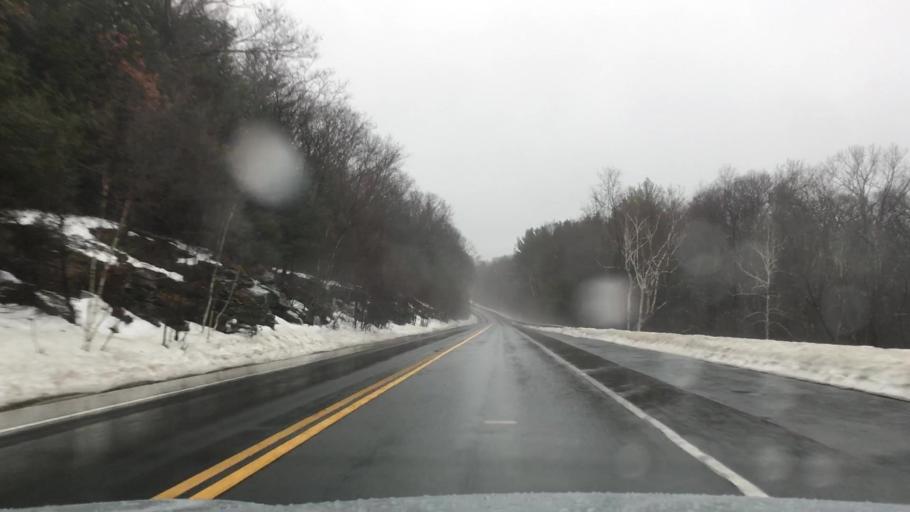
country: US
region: Massachusetts
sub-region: Hampshire County
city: Pelham
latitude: 42.4020
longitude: -72.4039
